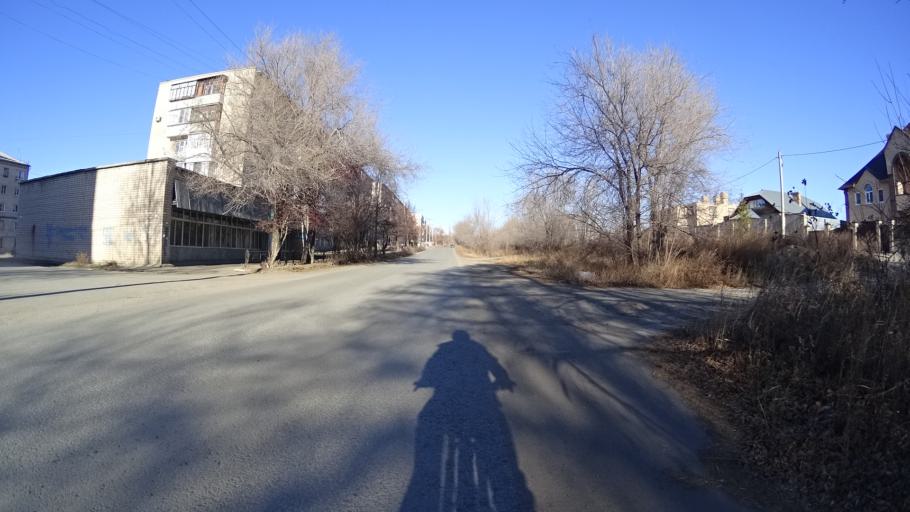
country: RU
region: Chelyabinsk
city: Troitsk
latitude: 54.0495
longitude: 61.6406
